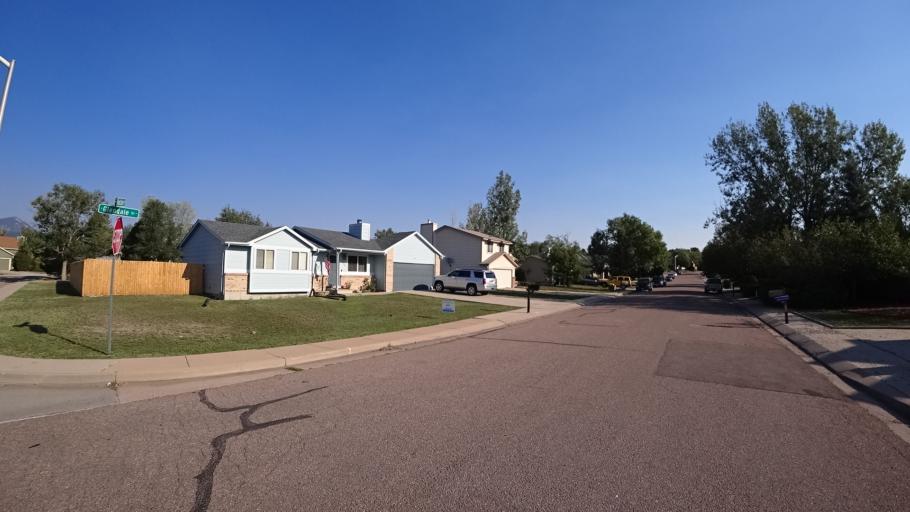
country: US
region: Colorado
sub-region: El Paso County
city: Stratmoor
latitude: 38.7745
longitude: -104.8041
